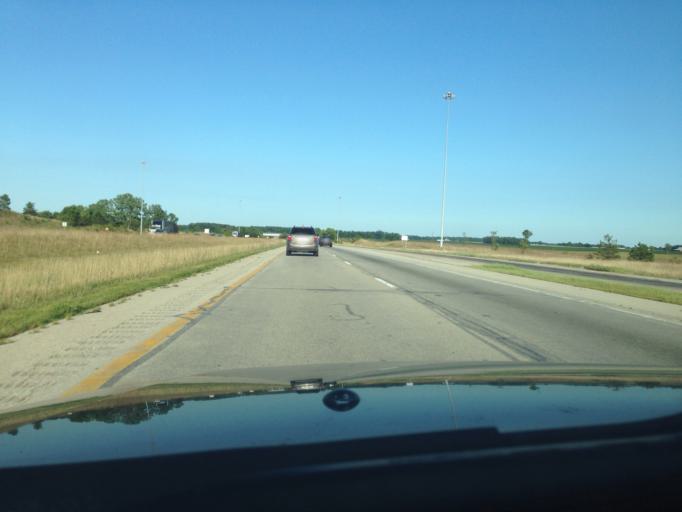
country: US
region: Ohio
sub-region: Preble County
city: New Paris
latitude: 39.8284
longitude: -84.7582
